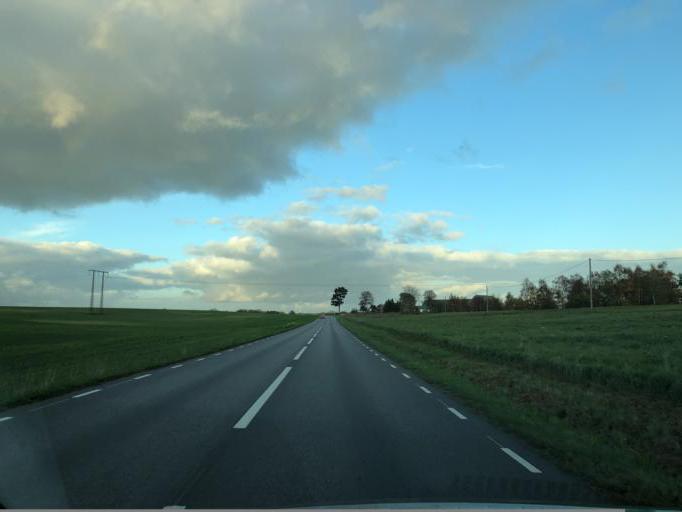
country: SE
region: Skane
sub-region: Svalovs Kommun
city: Teckomatorp
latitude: 55.8563
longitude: 13.1295
